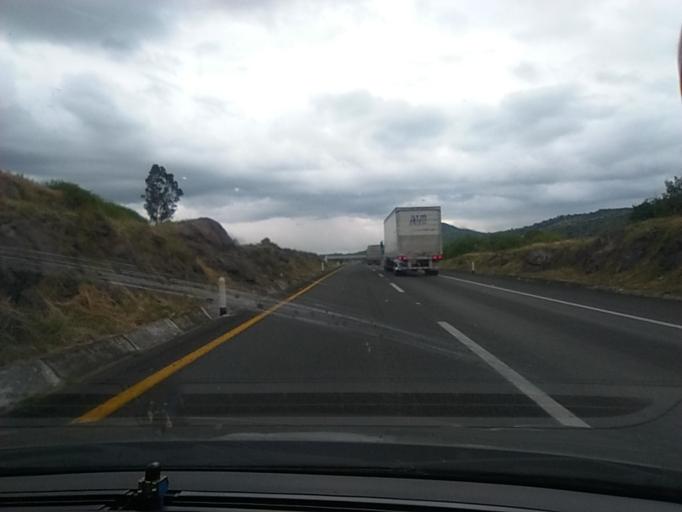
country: MX
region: Jalisco
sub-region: Zapotlan del Rey
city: Zapotlan del Rey
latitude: 20.5285
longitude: -103.0063
